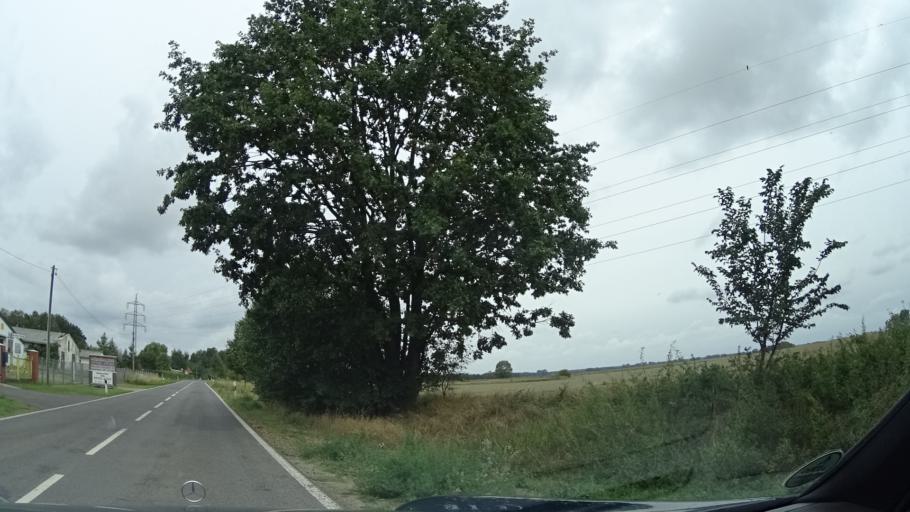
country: DE
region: Brandenburg
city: Dabergotz
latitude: 52.9311
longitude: 12.7434
